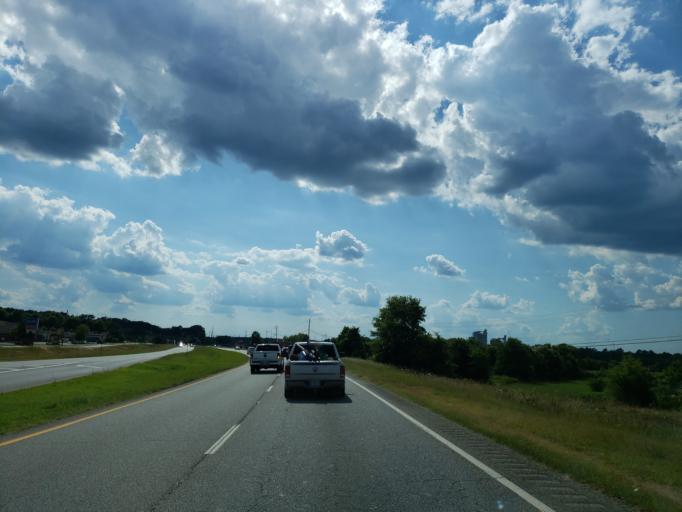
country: US
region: Georgia
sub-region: Polk County
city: Rockmart
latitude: 34.0101
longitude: -85.0333
